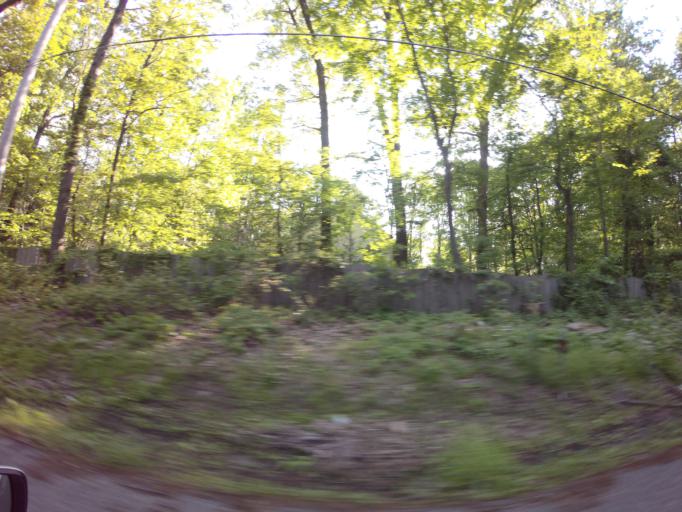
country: US
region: Maryland
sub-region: Baltimore County
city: Mays Chapel
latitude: 39.4442
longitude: -76.6841
